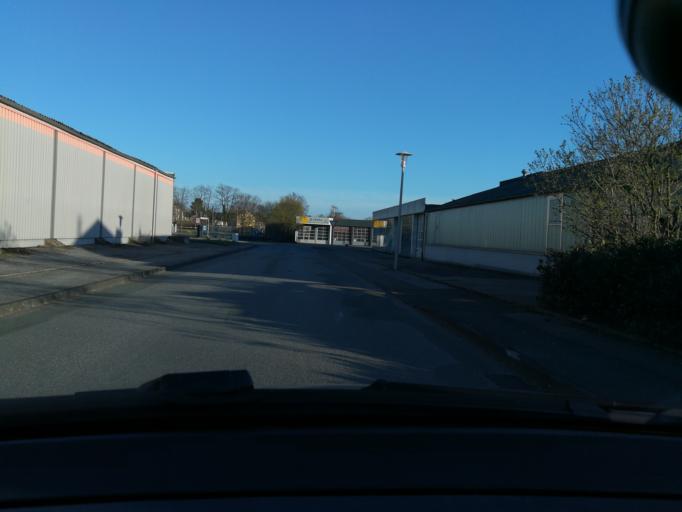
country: DE
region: North Rhine-Westphalia
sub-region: Regierungsbezirk Detmold
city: Oerlinghausen
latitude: 51.9555
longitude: 8.5755
